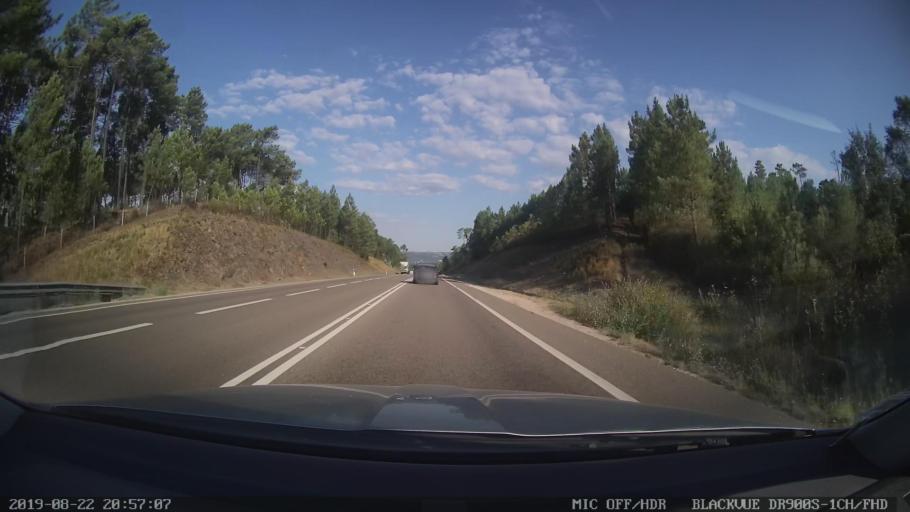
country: PT
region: Castelo Branco
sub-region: Serta
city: Serta
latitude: 39.7919
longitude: -8.0607
